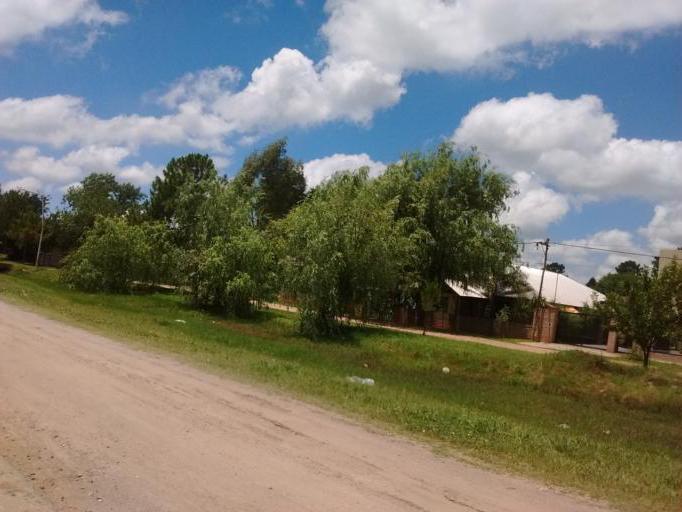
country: AR
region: Santa Fe
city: Funes
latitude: -32.9235
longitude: -60.7926
